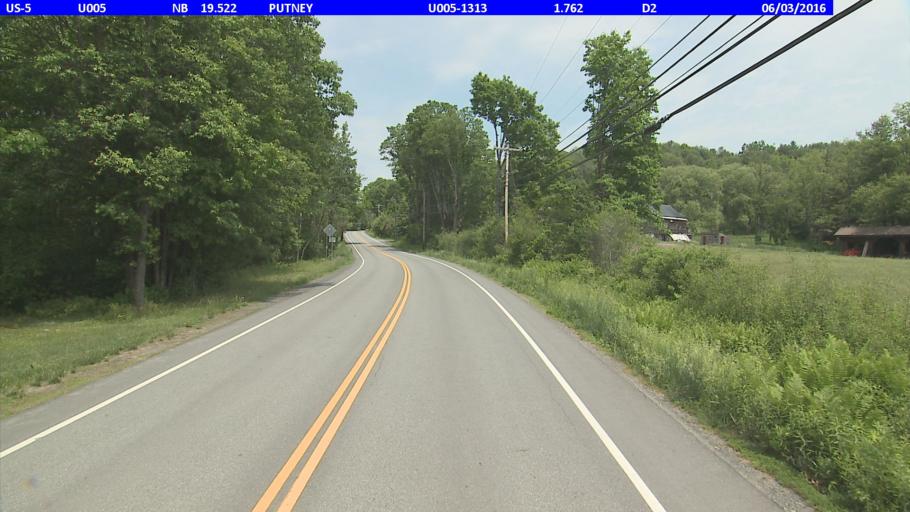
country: US
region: New Hampshire
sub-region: Cheshire County
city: Westmoreland
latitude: 42.9859
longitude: -72.5075
